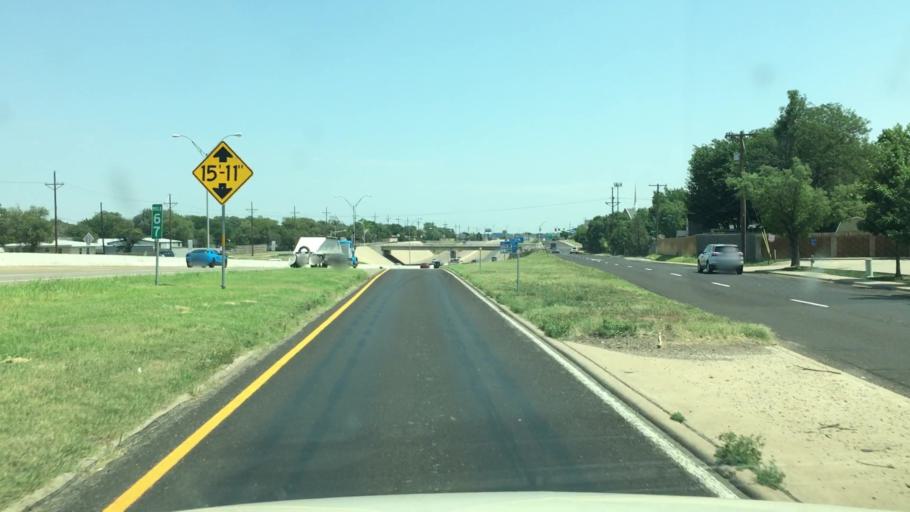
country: US
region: Texas
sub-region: Potter County
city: Amarillo
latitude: 35.1906
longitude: -101.8968
